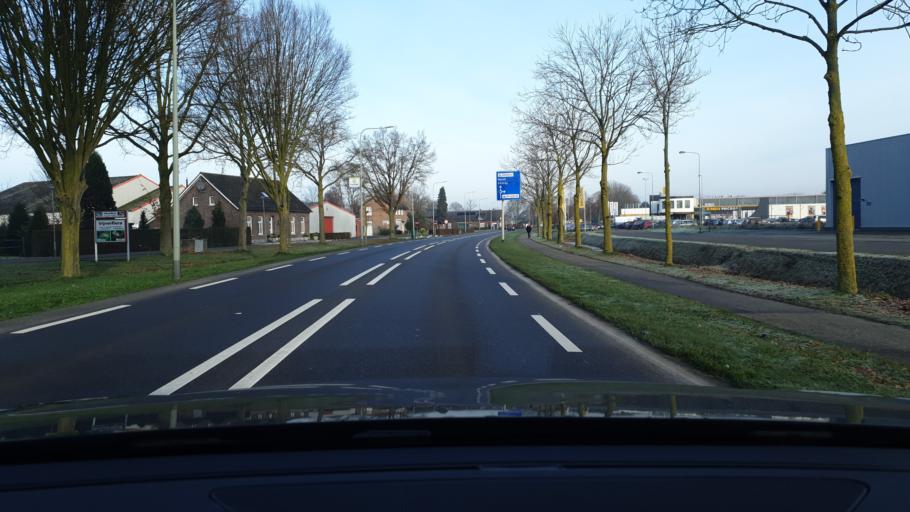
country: NL
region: Limburg
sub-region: Gemeente Peel en Maas
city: Maasbree
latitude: 51.4228
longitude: 6.0349
